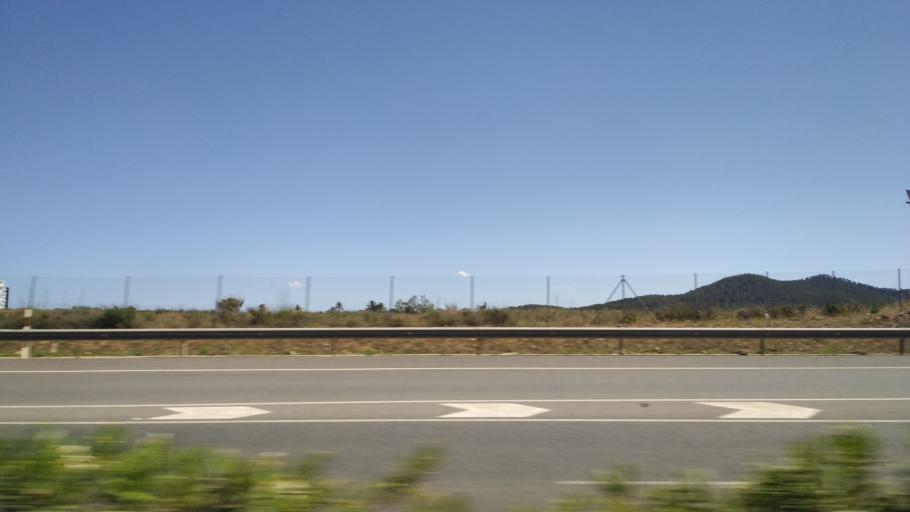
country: ES
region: Balearic Islands
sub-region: Illes Balears
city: Ibiza
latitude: 38.8870
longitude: 1.3979
